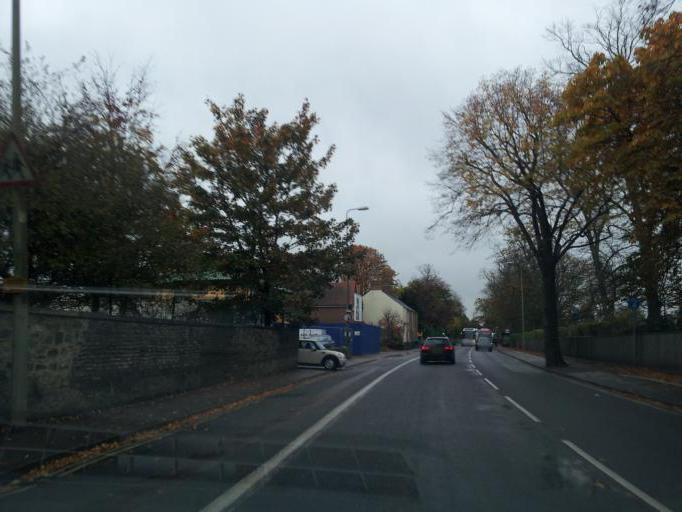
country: GB
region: England
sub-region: Oxfordshire
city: Oxford
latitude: 51.7782
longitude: -1.2707
